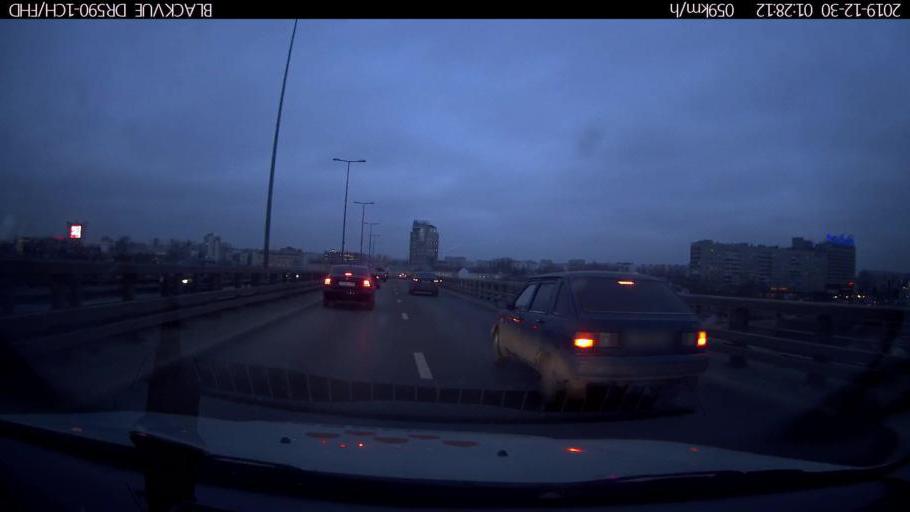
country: RU
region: Nizjnij Novgorod
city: Nizhniy Novgorod
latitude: 56.3222
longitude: 43.9588
